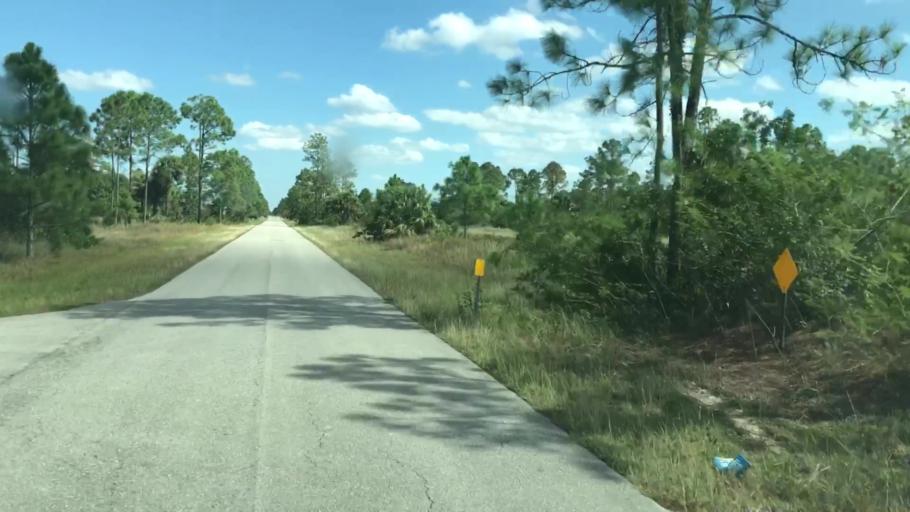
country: US
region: Florida
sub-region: Lee County
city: Lehigh Acres
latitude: 26.6283
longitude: -81.6394
